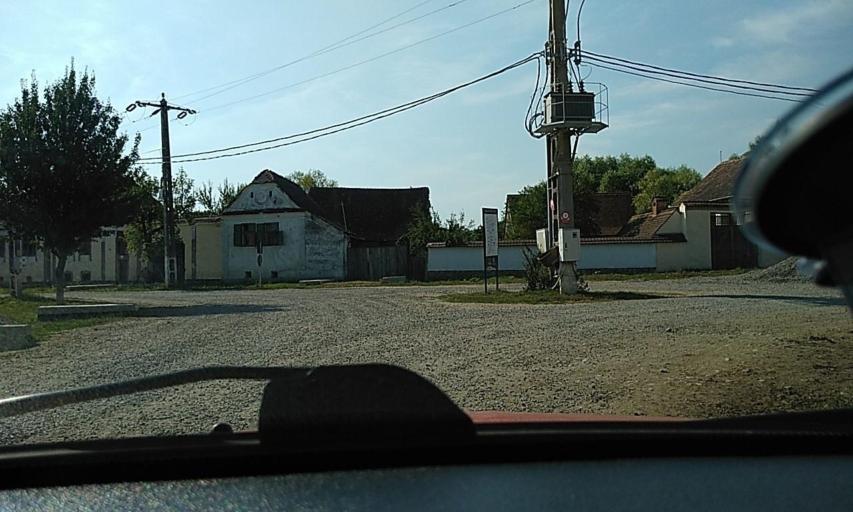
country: RO
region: Brasov
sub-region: Oras Rupea
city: Fiser
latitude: 46.0570
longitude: 25.0973
